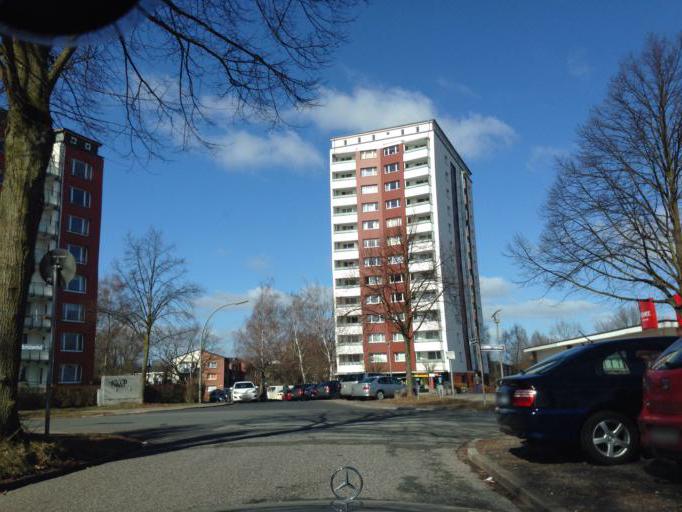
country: DE
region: Hamburg
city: Marienthal
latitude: 53.5950
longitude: 10.0856
